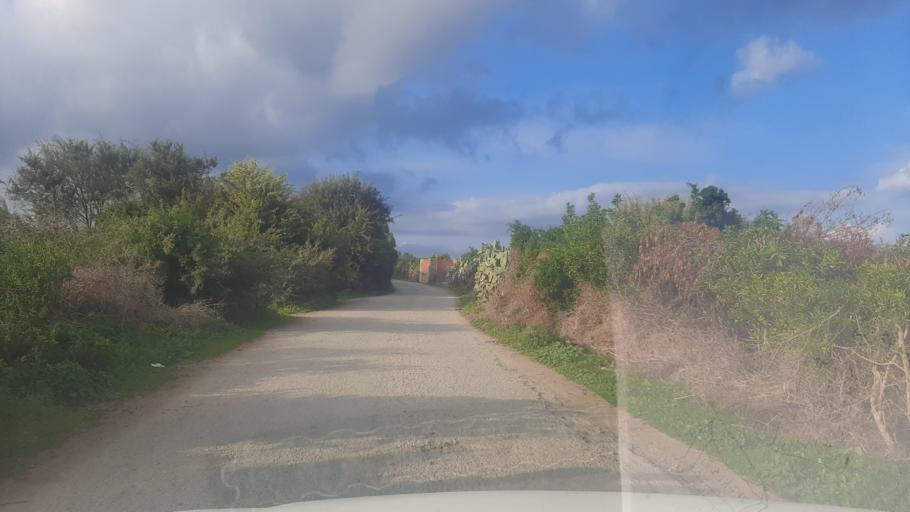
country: TN
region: Nabul
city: Manzil Bu Zalafah
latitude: 36.7115
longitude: 10.5002
